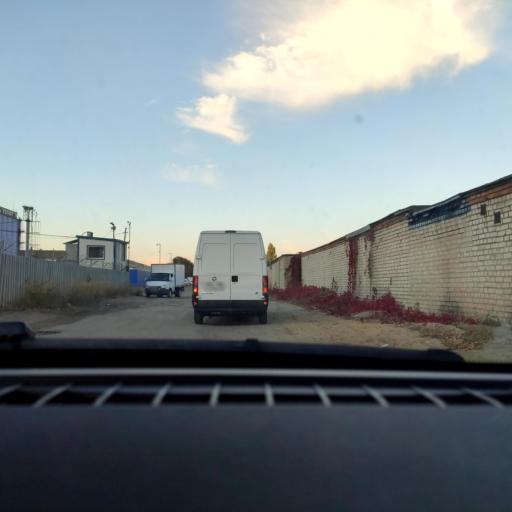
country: RU
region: Voronezj
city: Maslovka
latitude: 51.6376
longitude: 39.2789
